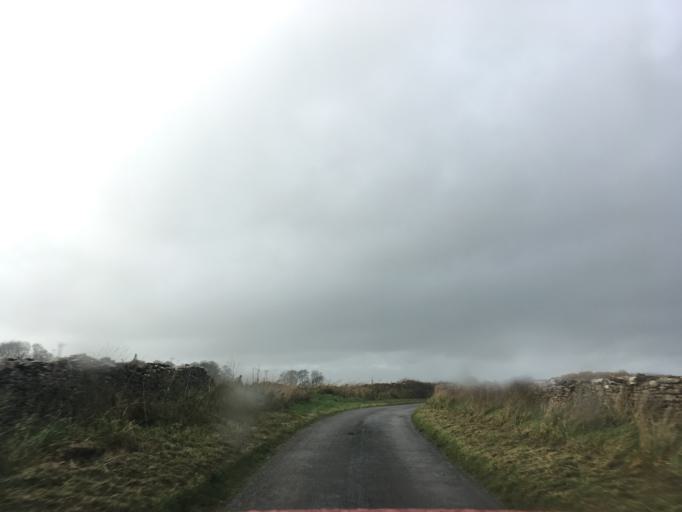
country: GB
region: England
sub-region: South Gloucestershire
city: Cold Ashton
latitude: 51.4694
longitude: -2.3605
